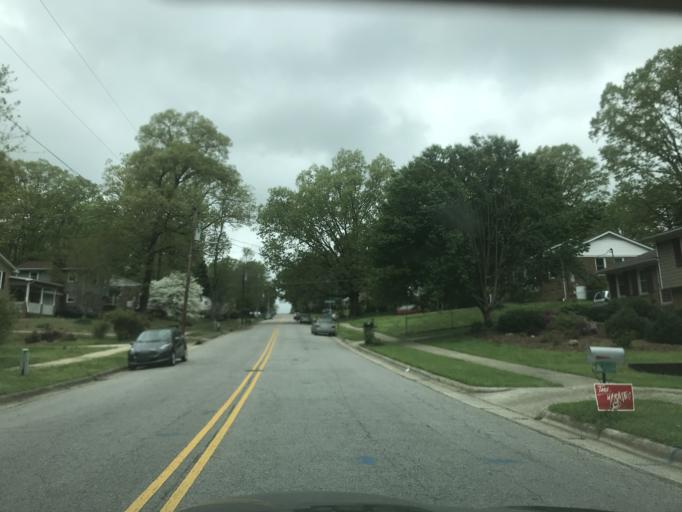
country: US
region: North Carolina
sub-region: Wake County
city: West Raleigh
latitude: 35.7512
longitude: -78.6732
